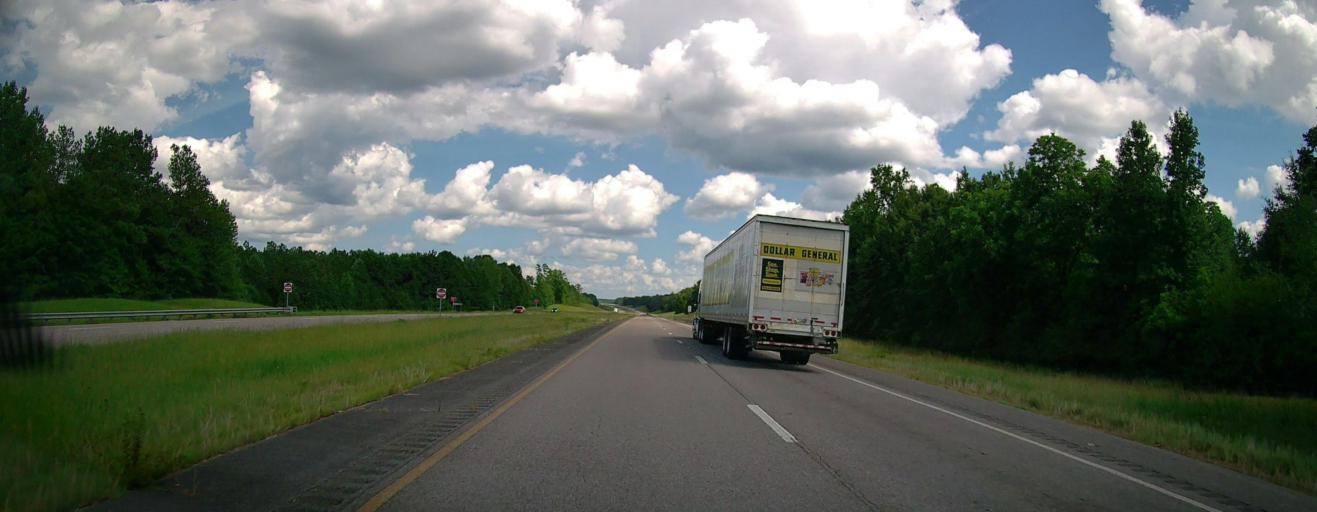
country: US
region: Mississippi
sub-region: Lowndes County
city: New Hope
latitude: 33.4864
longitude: -88.2673
